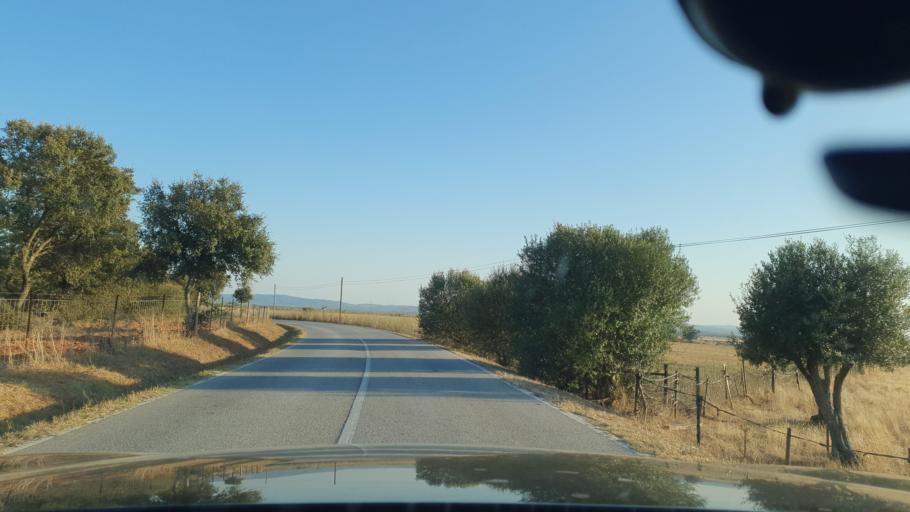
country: PT
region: Evora
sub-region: Estremoz
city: Estremoz
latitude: 38.9038
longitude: -7.6678
